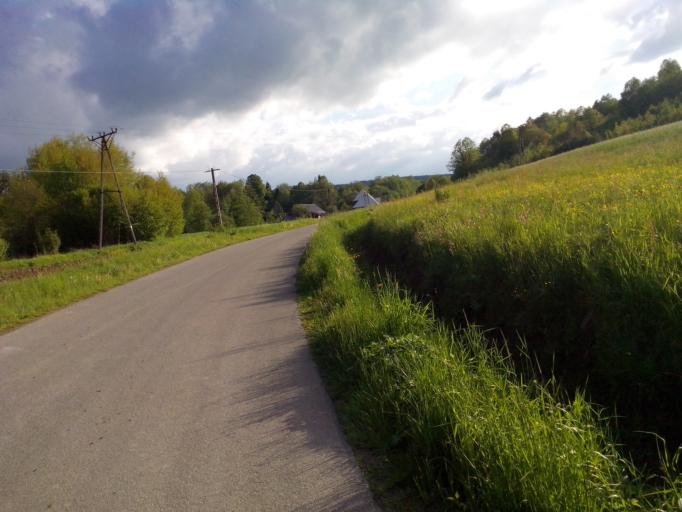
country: PL
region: Subcarpathian Voivodeship
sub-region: Powiat strzyzowski
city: Strzyzow
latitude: 49.8017
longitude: 21.8280
